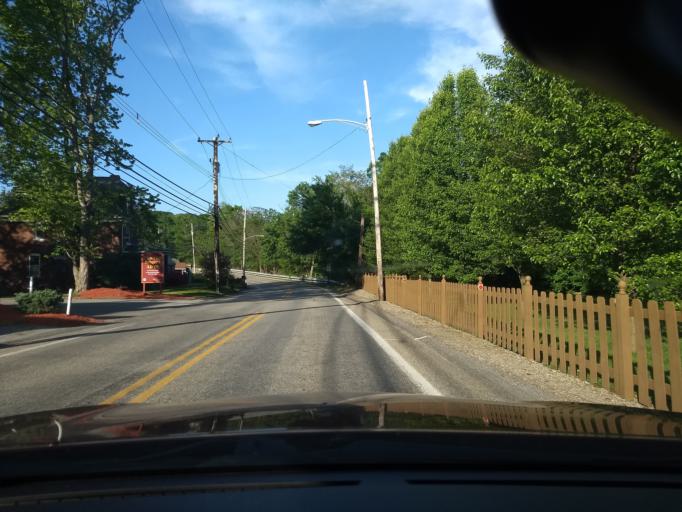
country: US
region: Pennsylvania
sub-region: Allegheny County
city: Versailles
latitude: 40.3191
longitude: -79.8230
